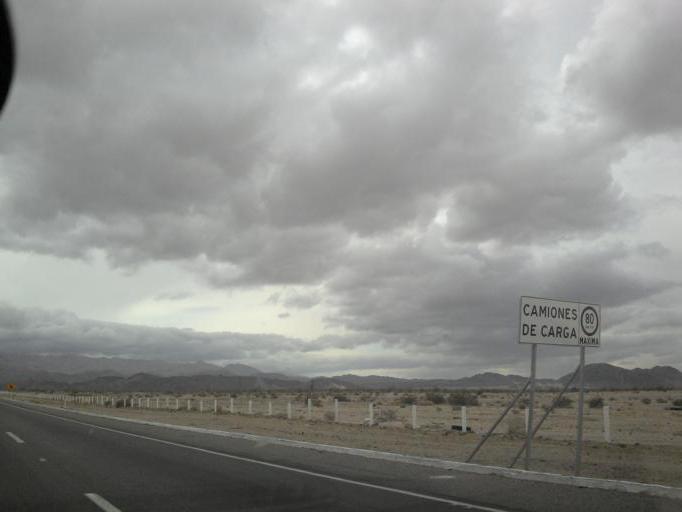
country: MX
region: Baja California
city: Progreso
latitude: 32.5648
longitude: -115.8801
